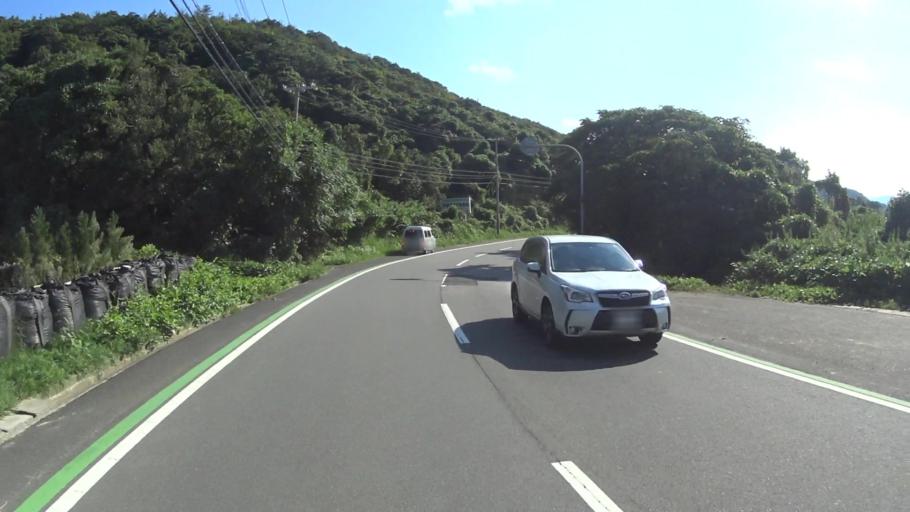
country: JP
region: Kyoto
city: Miyazu
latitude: 35.7252
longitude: 135.0859
